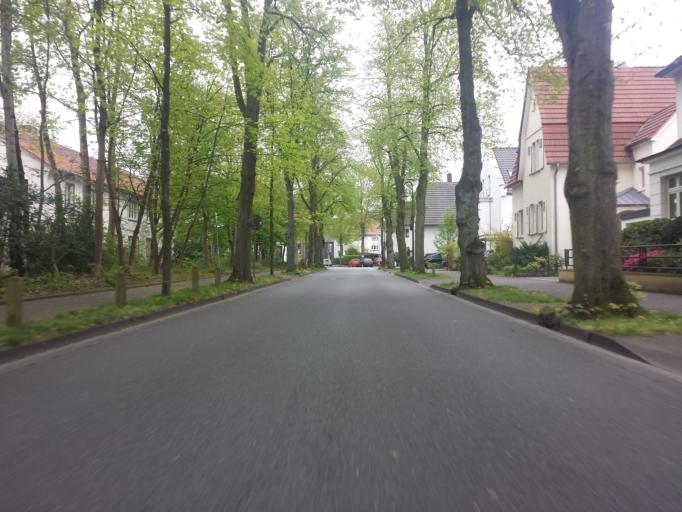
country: DE
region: North Rhine-Westphalia
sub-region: Regierungsbezirk Detmold
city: Guetersloh
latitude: 51.8971
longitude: 8.3829
